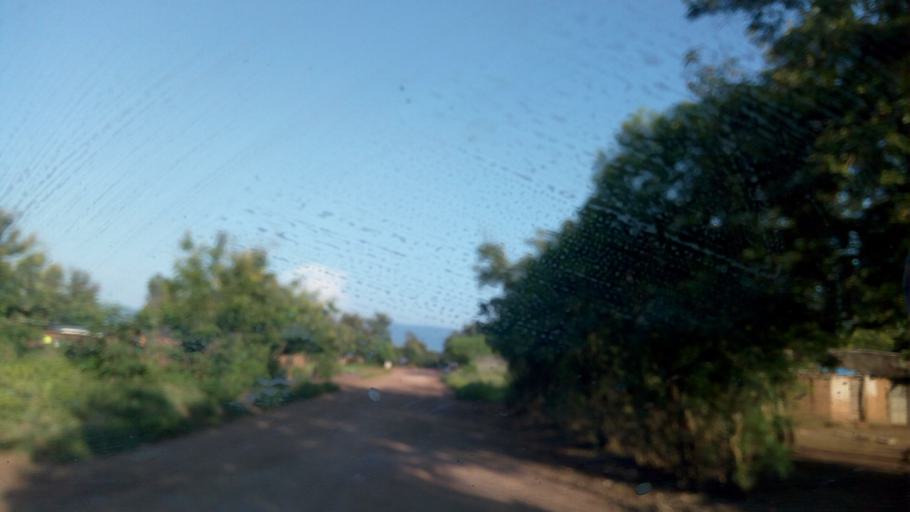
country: BI
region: Bururi
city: Rumonge
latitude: -4.1984
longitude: 29.0336
